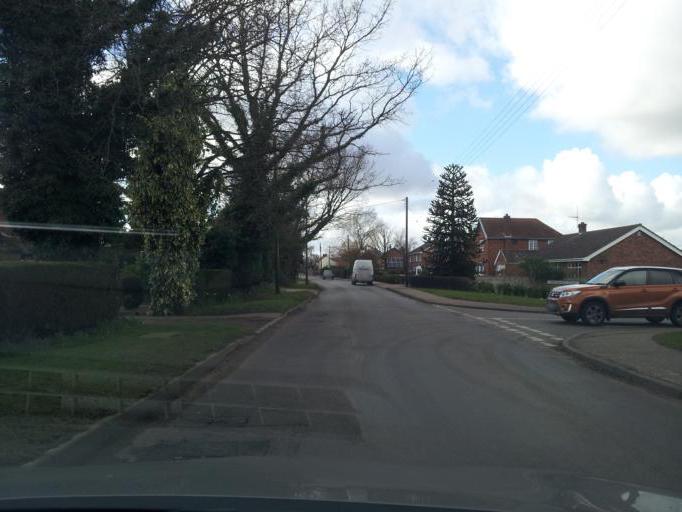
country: GB
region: England
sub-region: Norfolk
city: Mattishall
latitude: 52.6605
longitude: 1.0207
